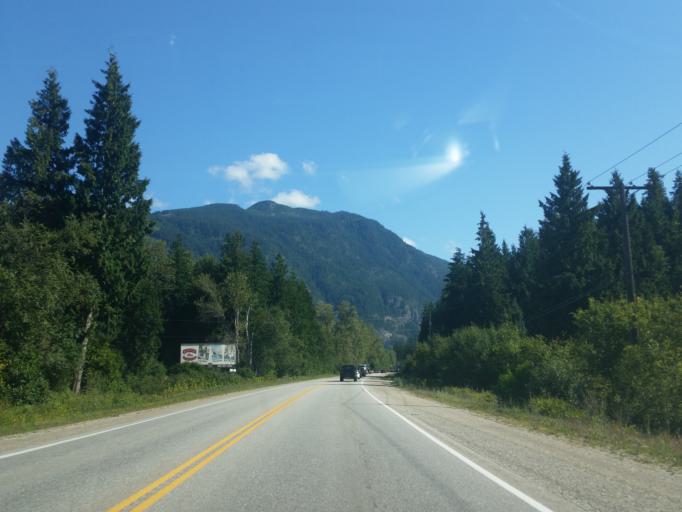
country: CA
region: British Columbia
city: Sicamous
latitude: 50.8740
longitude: -118.9240
